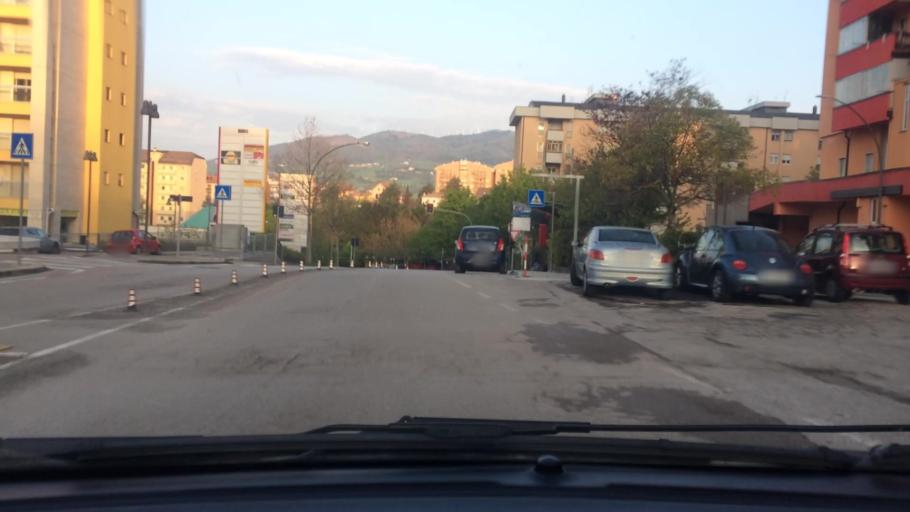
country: IT
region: Basilicate
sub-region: Provincia di Potenza
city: Potenza
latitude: 40.6431
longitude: 15.7906
